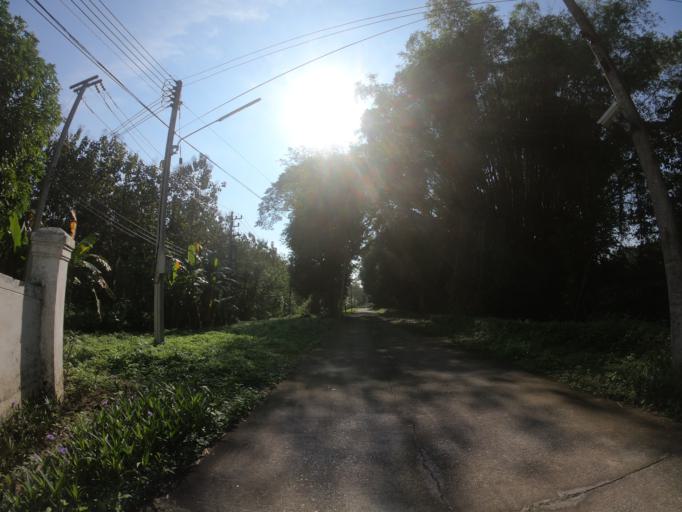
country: TH
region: Chiang Mai
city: Chiang Mai
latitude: 18.7373
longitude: 98.9840
